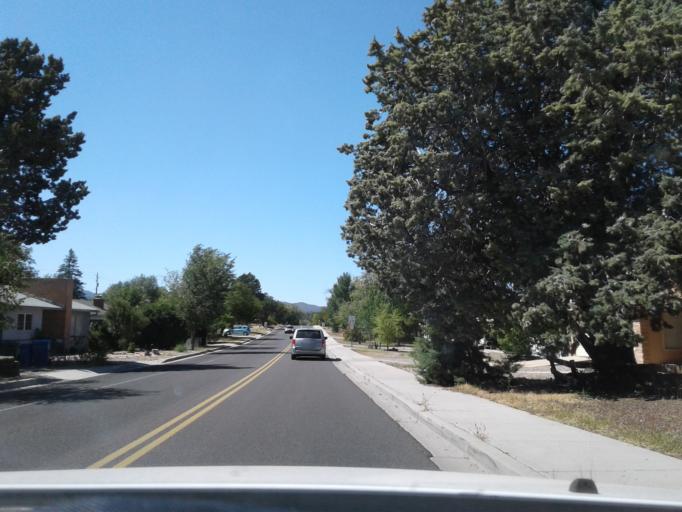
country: US
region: Arizona
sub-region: Yavapai County
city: Prescott
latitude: 34.5708
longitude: -112.4738
